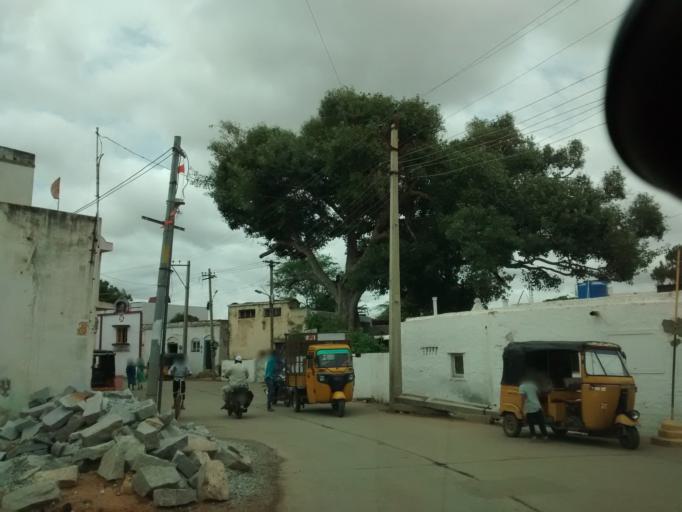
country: IN
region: Andhra Pradesh
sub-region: Anantapur
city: Hindupur
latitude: 13.8244
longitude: 77.4912
